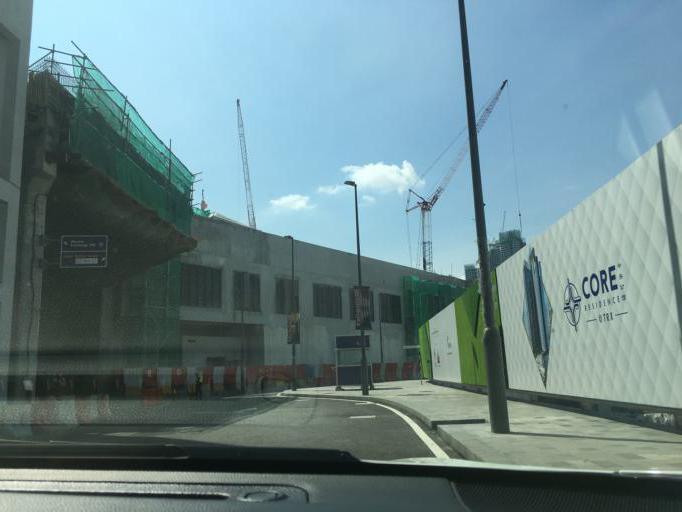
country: MY
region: Kuala Lumpur
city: Kuala Lumpur
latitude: 3.1419
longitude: 101.7168
